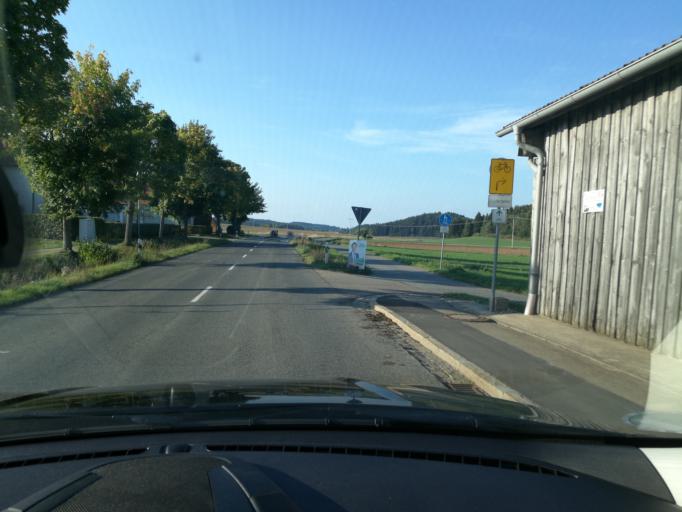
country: DE
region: Bavaria
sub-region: Upper Palatinate
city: Velburg
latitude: 49.2765
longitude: 11.6674
